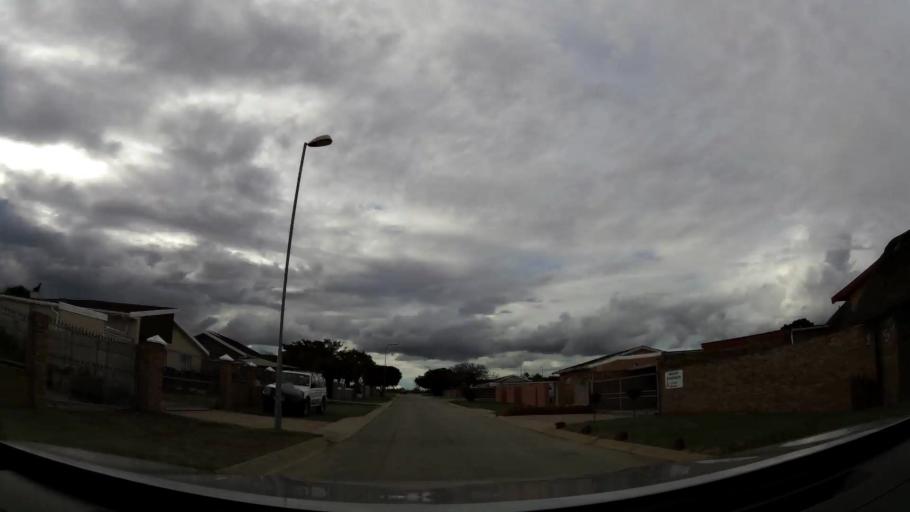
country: ZA
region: Eastern Cape
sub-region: Nelson Mandela Bay Metropolitan Municipality
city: Port Elizabeth
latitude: -33.9371
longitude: 25.4737
